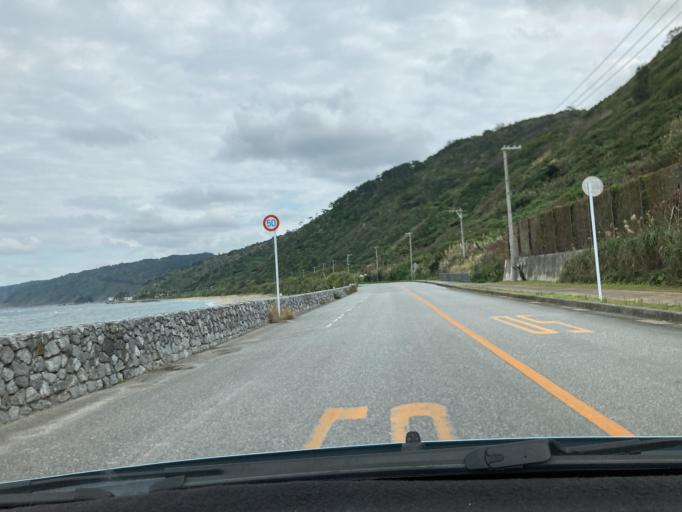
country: JP
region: Okinawa
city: Nago
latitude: 26.7751
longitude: 128.2058
